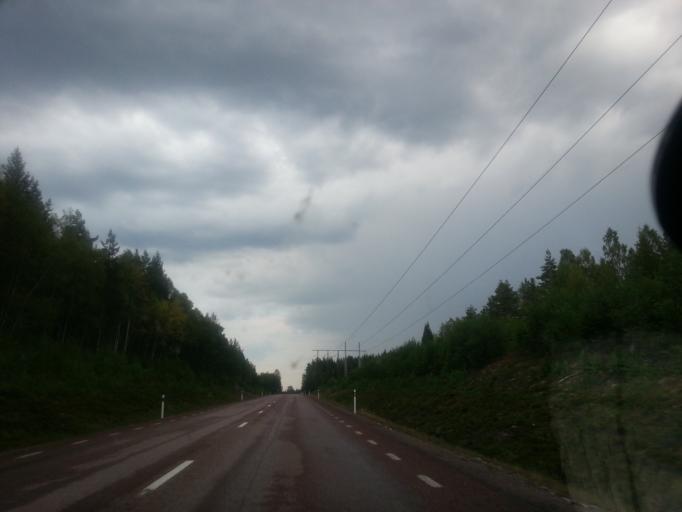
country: SE
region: Gaevleborg
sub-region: Hofors Kommun
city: Hofors
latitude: 60.5431
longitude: 16.4666
